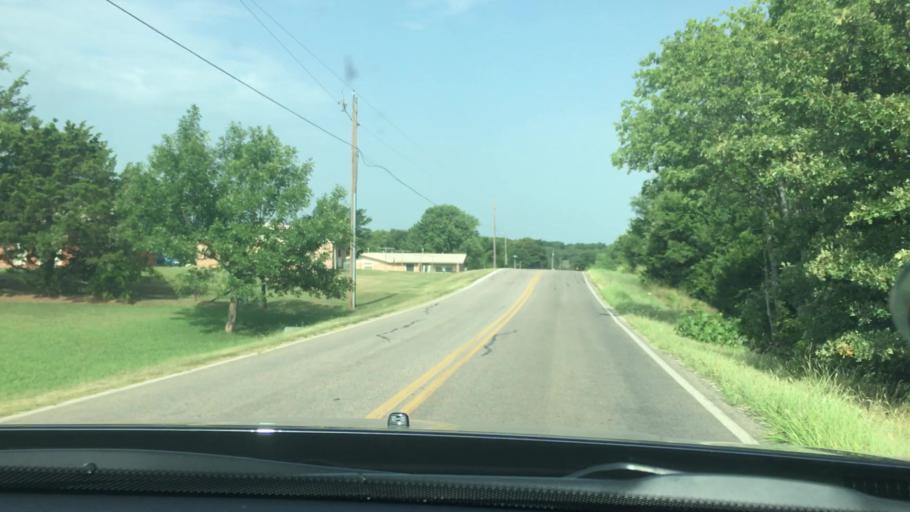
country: US
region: Oklahoma
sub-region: Pontotoc County
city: Byng
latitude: 34.8685
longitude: -96.6729
